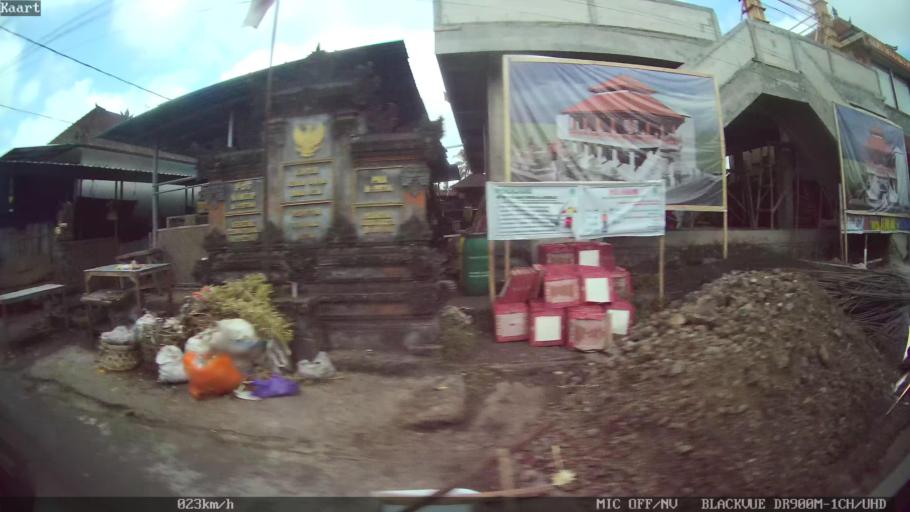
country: ID
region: Bali
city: Banjar Petak
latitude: -8.4464
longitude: 115.3190
